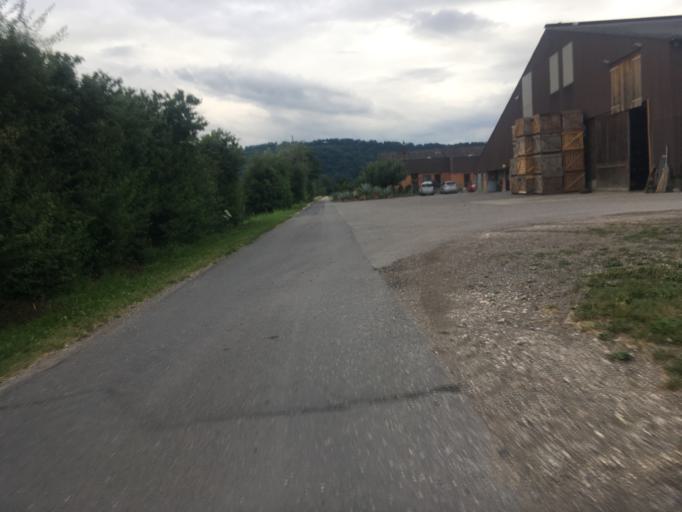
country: CH
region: Bern
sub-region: Seeland District
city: Ins
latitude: 46.9857
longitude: 7.1035
